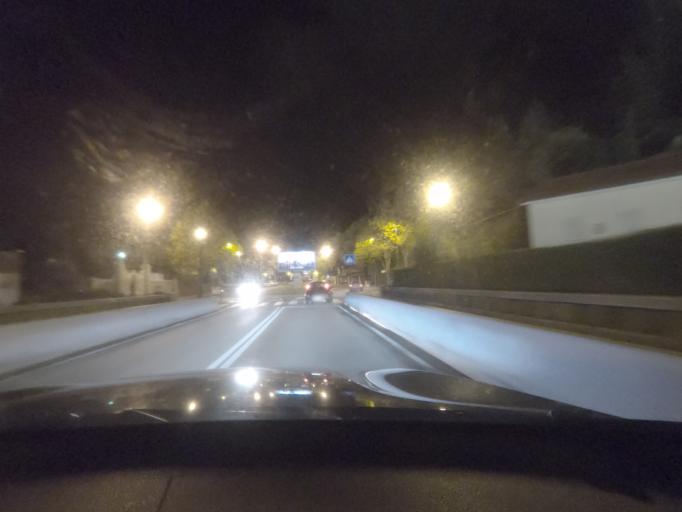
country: PT
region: Vila Real
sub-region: Vila Real
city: Vila Real
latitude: 41.2960
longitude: -7.7401
